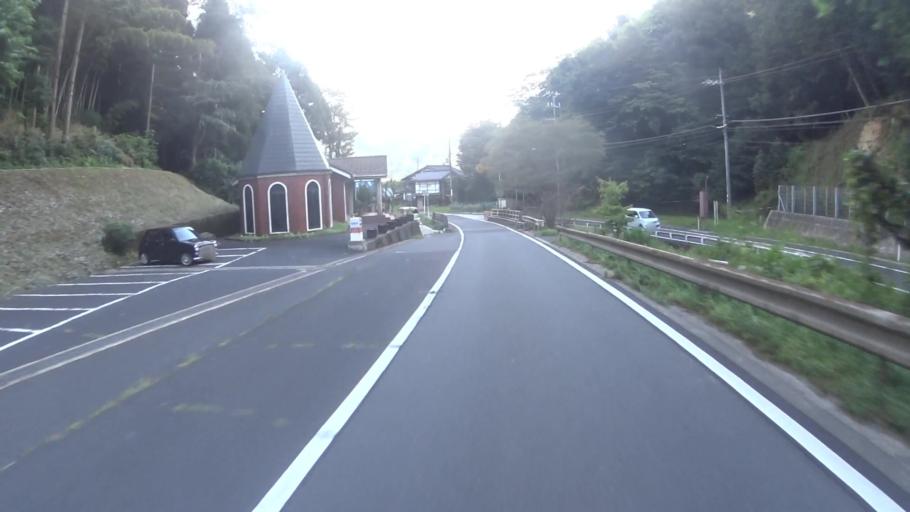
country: JP
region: Kyoto
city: Miyazu
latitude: 35.5412
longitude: 135.1105
